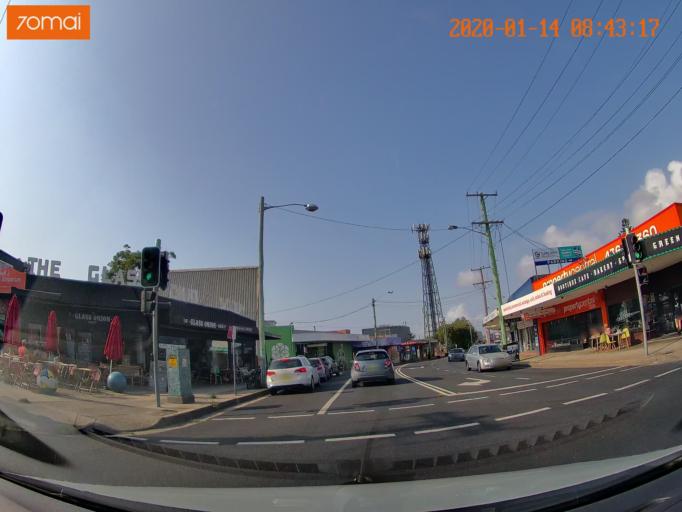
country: AU
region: New South Wales
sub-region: Wyong Shire
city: Long Jetty
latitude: -33.3574
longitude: 151.4858
